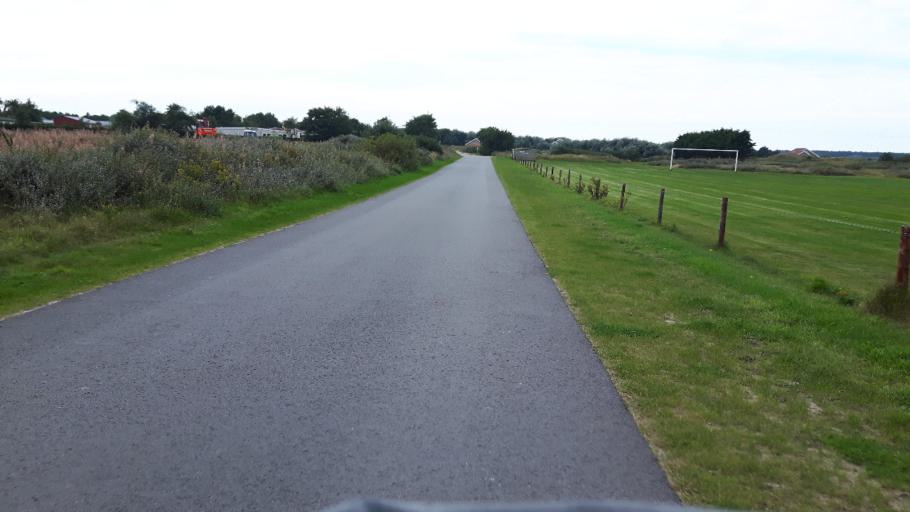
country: NL
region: Friesland
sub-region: Gemeente Ameland
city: Nes
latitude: 53.4534
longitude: 5.8187
